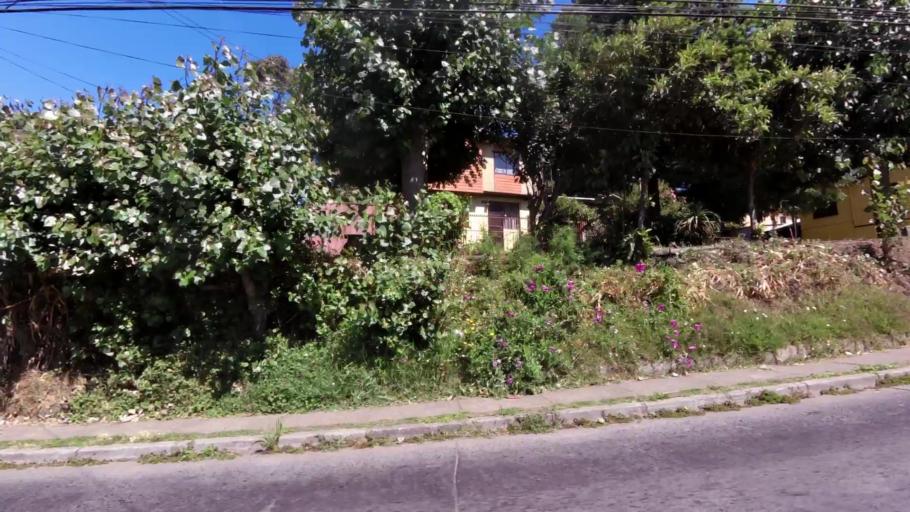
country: CL
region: Biobio
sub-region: Provincia de Concepcion
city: Concepcion
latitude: -36.8019
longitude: -73.0382
